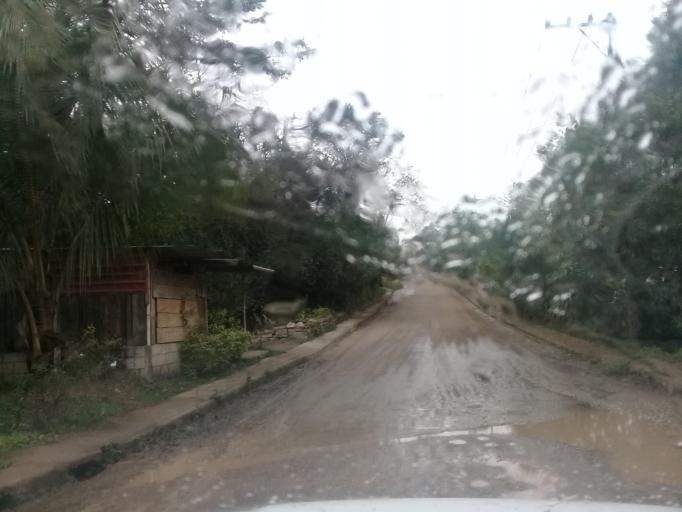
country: MX
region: Veracruz
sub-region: Amatlan de los Reyes
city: Trapiche Viejo
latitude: 18.8436
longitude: -96.9428
